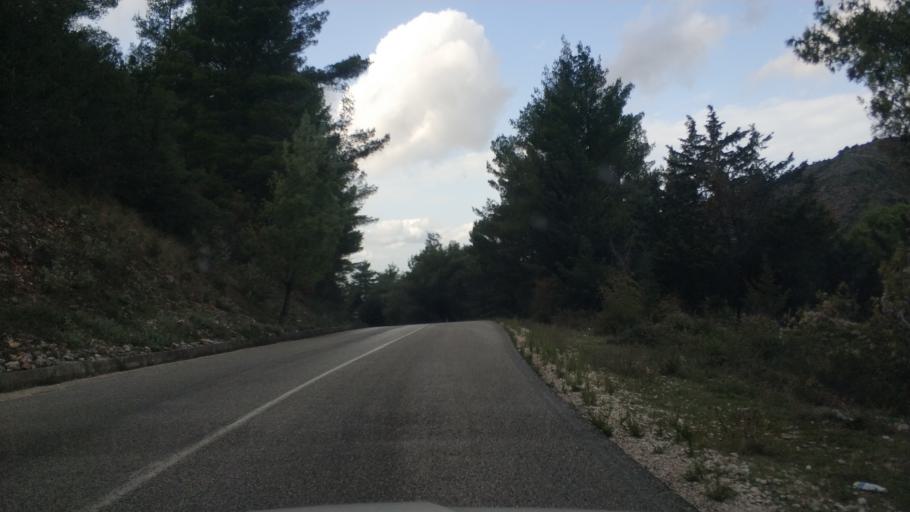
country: AL
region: Vlore
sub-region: Rrethi i Vlores
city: Orikum
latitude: 40.2515
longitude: 19.5390
